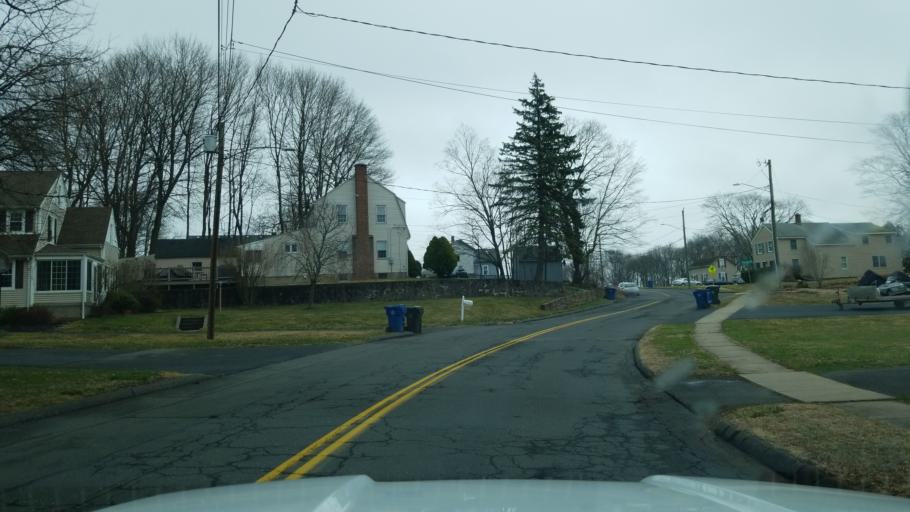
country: US
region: Connecticut
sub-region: Hartford County
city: Kensington
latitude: 41.6346
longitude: -72.7734
